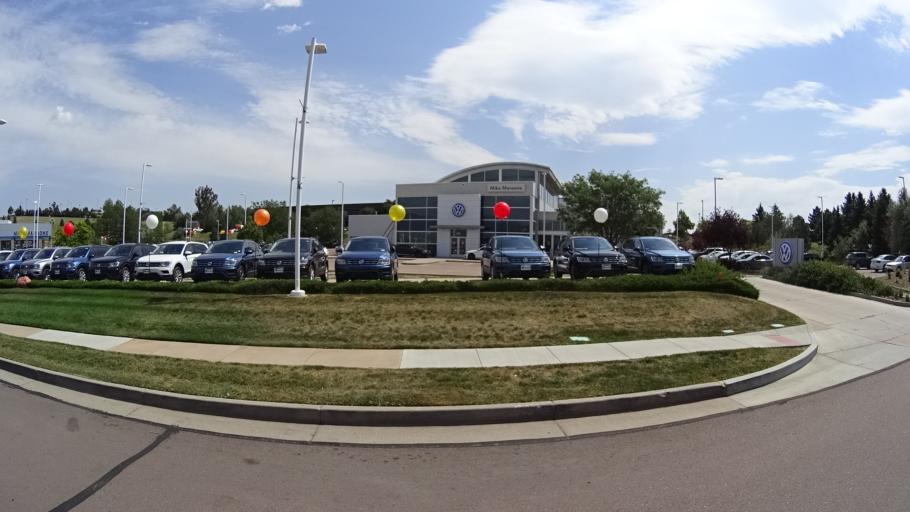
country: US
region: Colorado
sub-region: El Paso County
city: Air Force Academy
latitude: 38.9526
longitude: -104.7949
